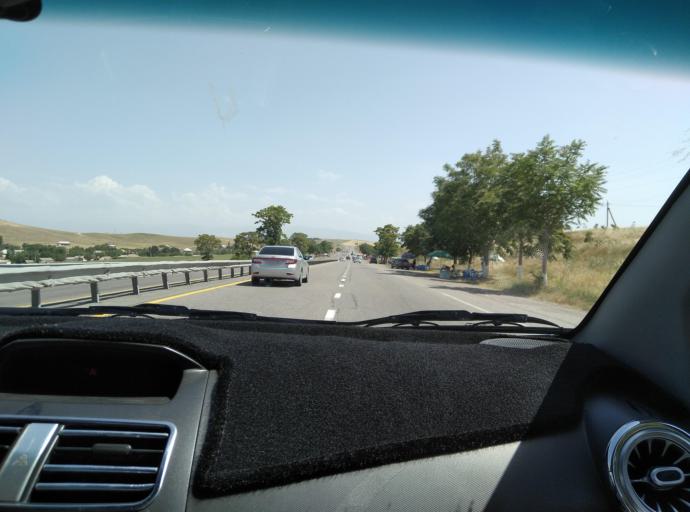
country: UZ
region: Toshkent
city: Ohangaron
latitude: 40.9813
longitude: 69.5399
